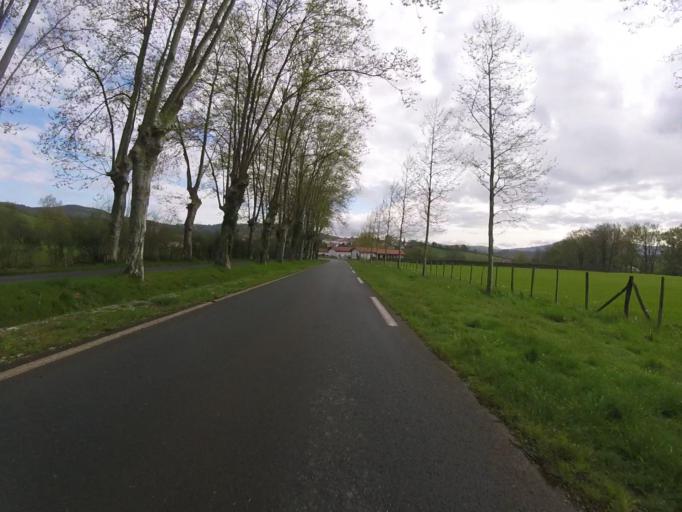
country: FR
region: Aquitaine
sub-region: Departement des Pyrenees-Atlantiques
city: Sare
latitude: 43.3081
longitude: -1.5870
